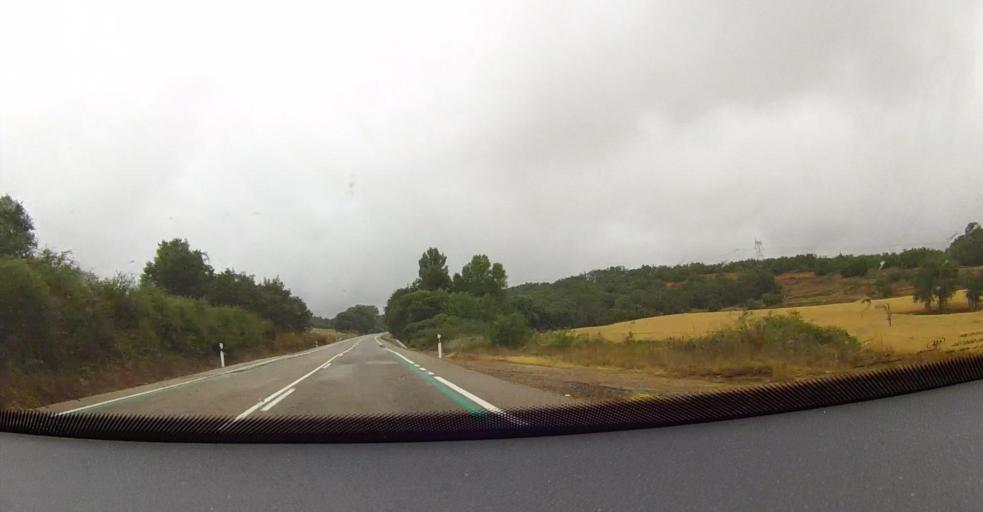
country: ES
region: Castille and Leon
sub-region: Provincia de Palencia
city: Saldana
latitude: 42.5569
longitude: -4.7429
